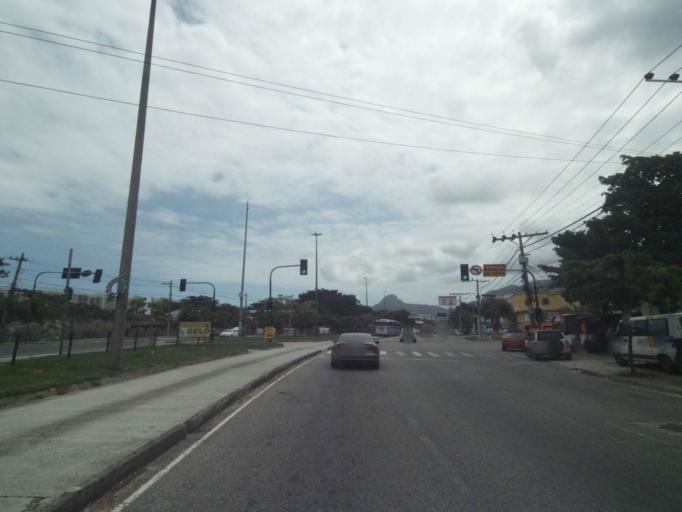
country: BR
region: Rio de Janeiro
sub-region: Nilopolis
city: Nilopolis
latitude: -22.9579
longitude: -43.3810
